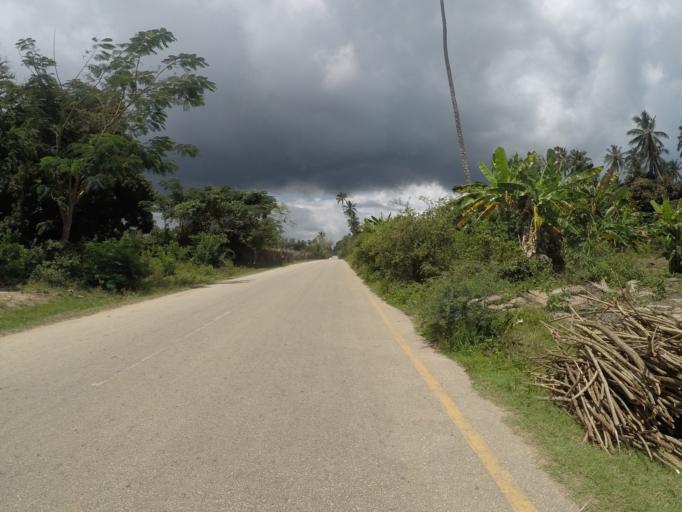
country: TZ
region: Zanzibar North
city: Mkokotoni
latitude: -5.9932
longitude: 39.1872
